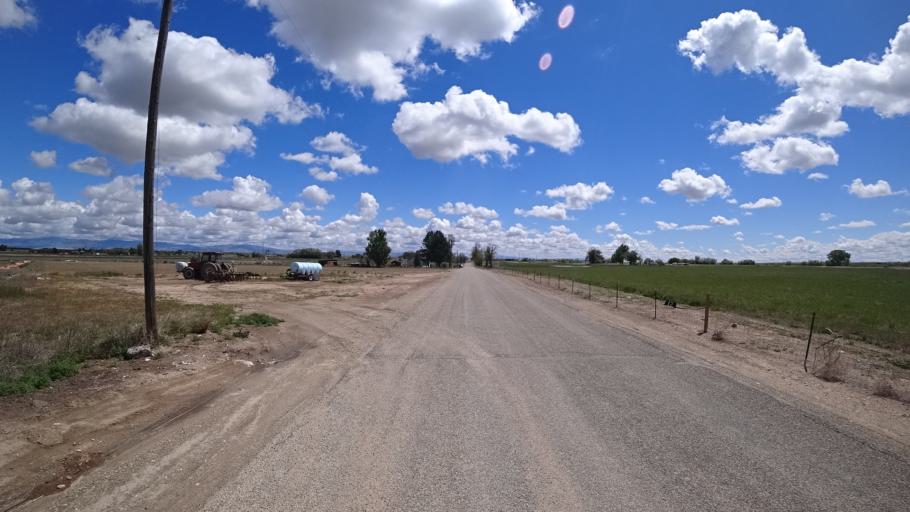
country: US
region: Idaho
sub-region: Ada County
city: Kuna
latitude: 43.4592
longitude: -116.3610
